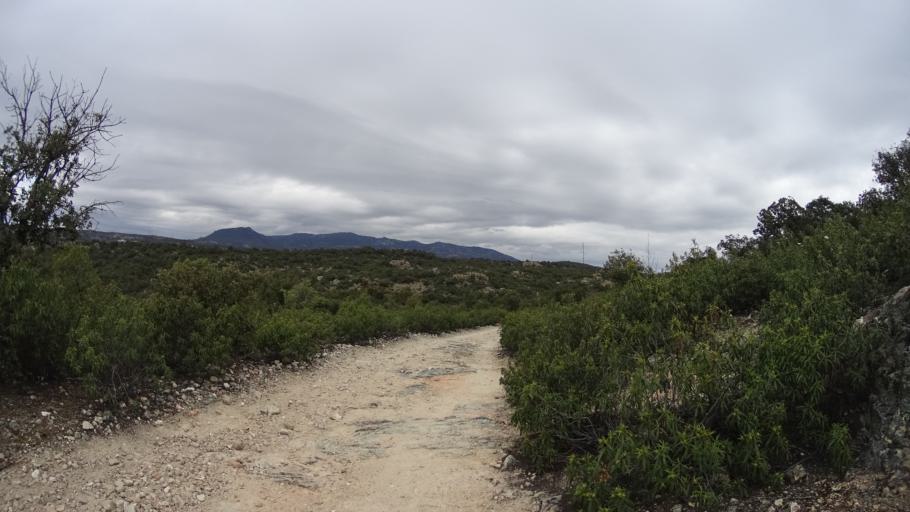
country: ES
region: Madrid
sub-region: Provincia de Madrid
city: Hoyo de Manzanares
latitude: 40.5956
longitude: -3.8860
